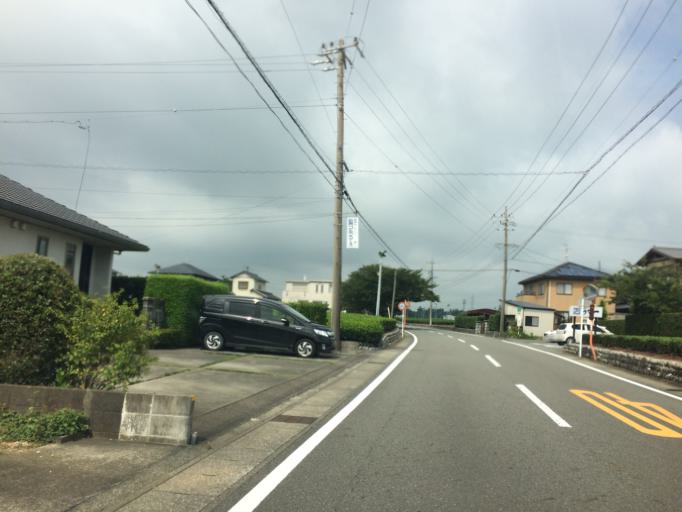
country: JP
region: Shizuoka
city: Shimada
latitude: 34.7989
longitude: 138.2183
